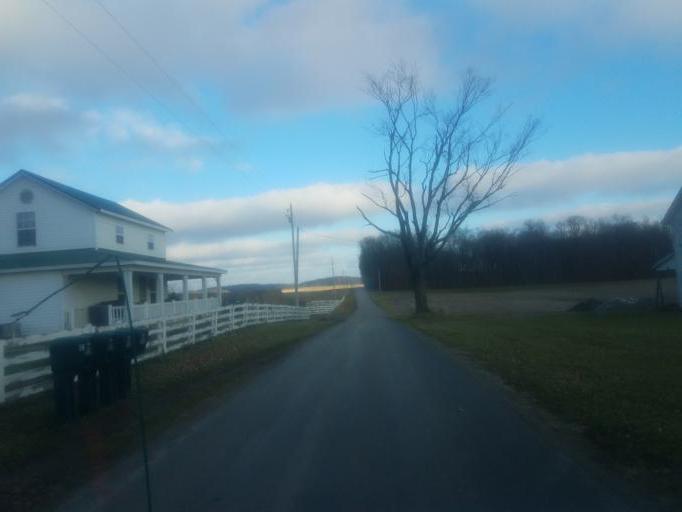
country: US
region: Ohio
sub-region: Ashland County
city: Loudonville
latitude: 40.6165
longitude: -82.3642
